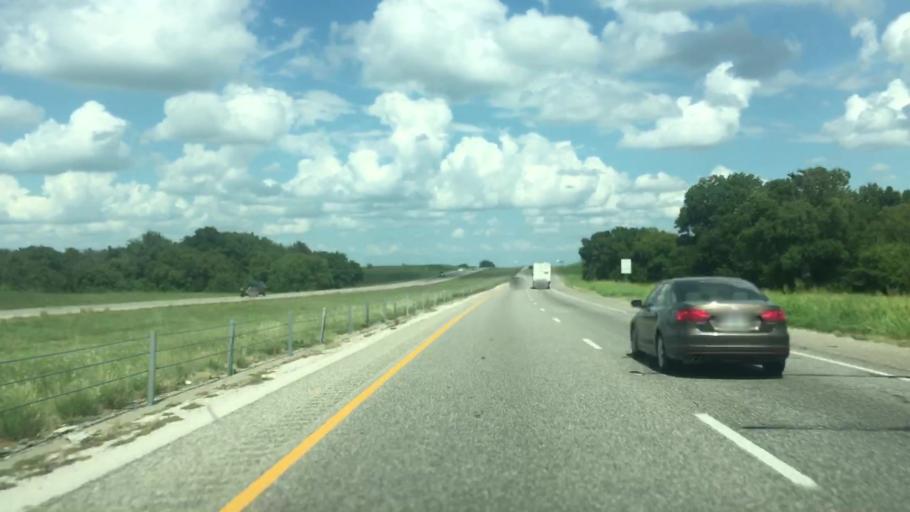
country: US
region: Texas
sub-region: Ellis County
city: Plum Grove
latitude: 32.1100
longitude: -97.0008
